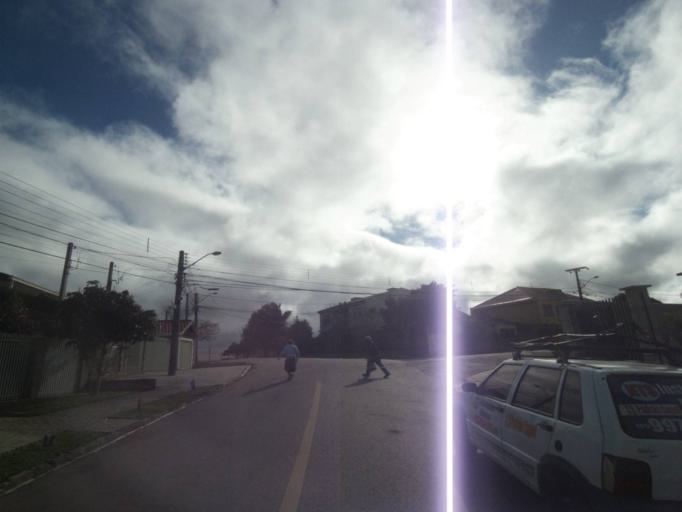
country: BR
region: Parana
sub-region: Sao Jose Dos Pinhais
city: Sao Jose dos Pinhais
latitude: -25.5206
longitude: -49.3008
